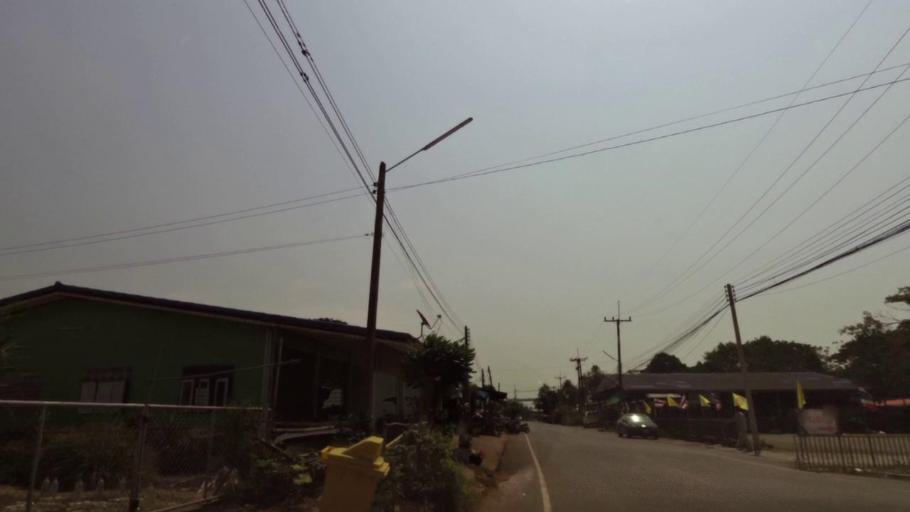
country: TH
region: Chanthaburi
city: Tha Mai
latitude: 12.5316
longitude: 101.9539
